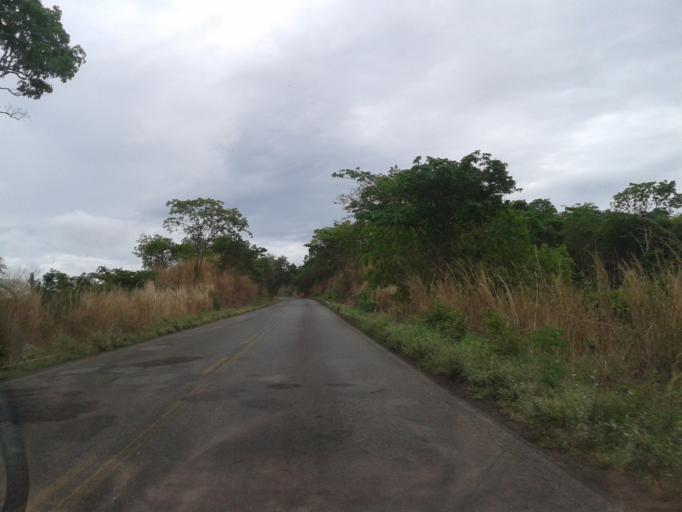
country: BR
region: Goias
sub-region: Buriti Alegre
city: Buriti Alegre
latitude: -18.0580
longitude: -48.7350
